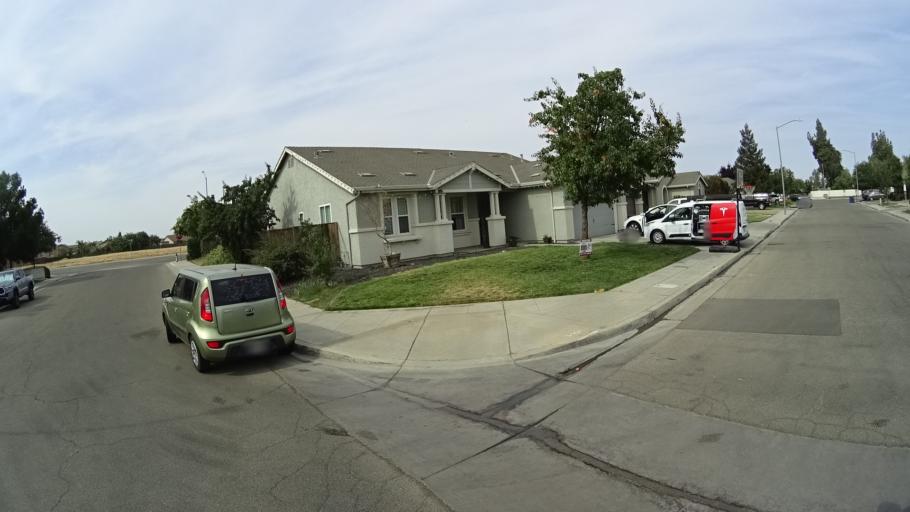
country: US
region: California
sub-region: Fresno County
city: West Park
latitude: 36.7651
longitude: -119.8875
